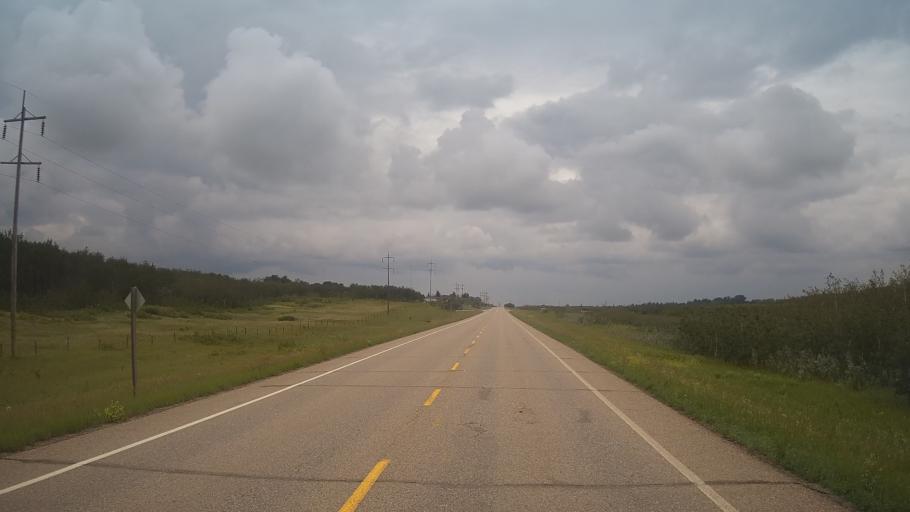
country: CA
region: Alberta
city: Wainwright
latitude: 52.5604
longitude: -111.0429
